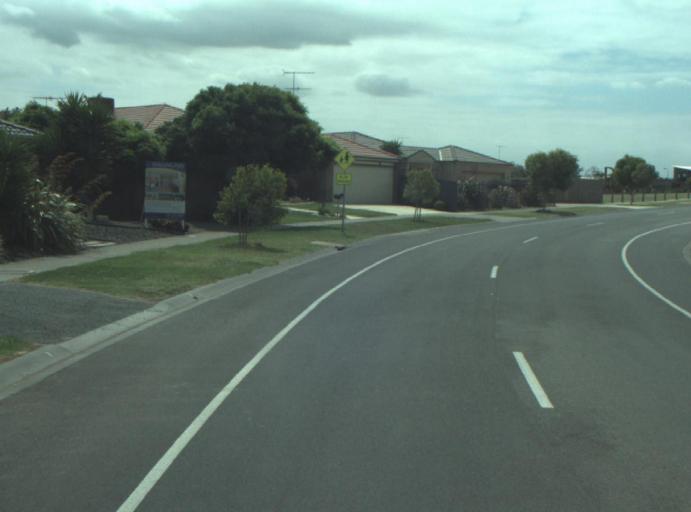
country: AU
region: Victoria
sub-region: Greater Geelong
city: Clifton Springs
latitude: -38.2551
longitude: 144.5474
